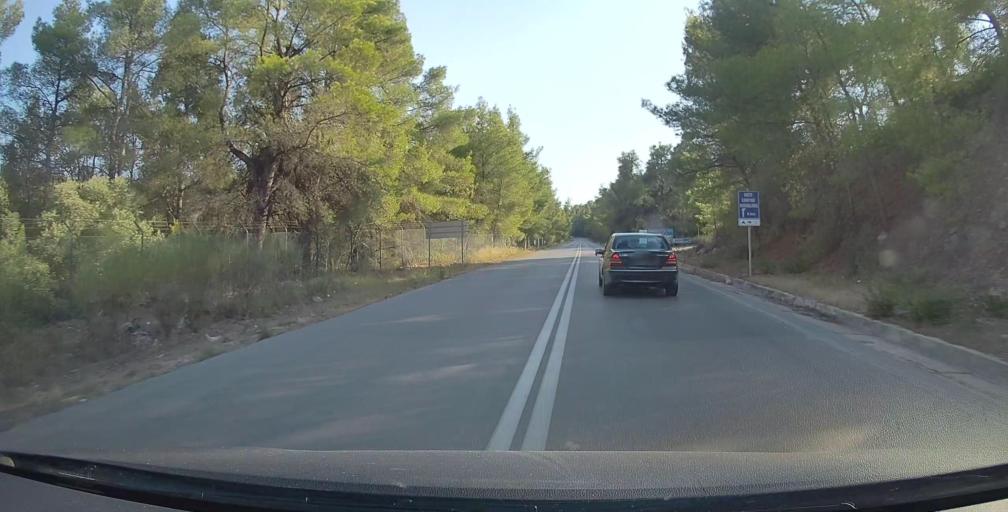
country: GR
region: Central Macedonia
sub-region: Nomos Chalkidikis
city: Neos Marmaras
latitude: 40.0696
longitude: 23.8047
